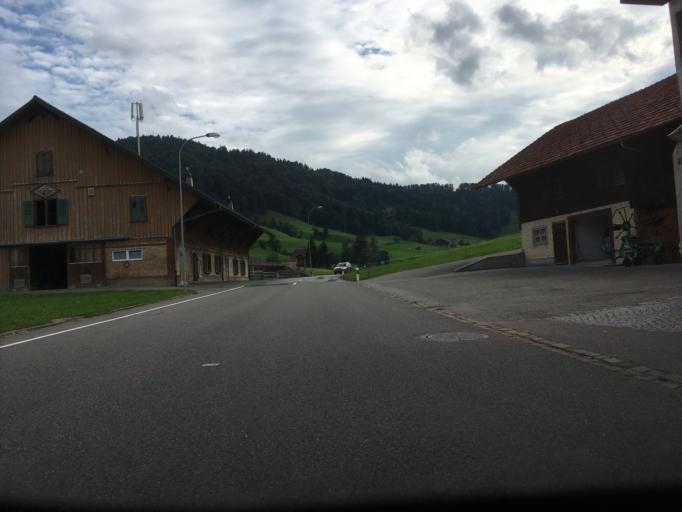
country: CH
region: Thurgau
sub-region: Muenchwilen District
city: Fischingen
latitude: 47.3709
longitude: 8.9850
